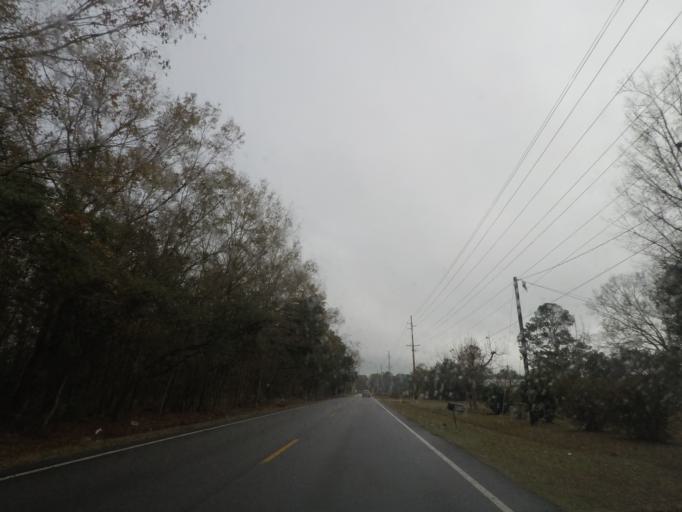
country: US
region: South Carolina
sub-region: Charleston County
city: Meggett
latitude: 32.6643
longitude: -80.3418
